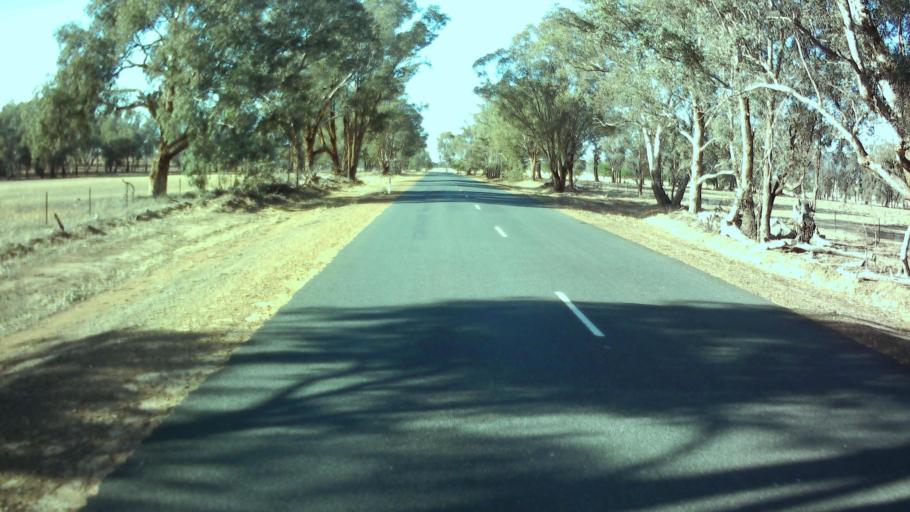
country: AU
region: New South Wales
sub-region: Weddin
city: Grenfell
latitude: -33.9401
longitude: 148.1367
